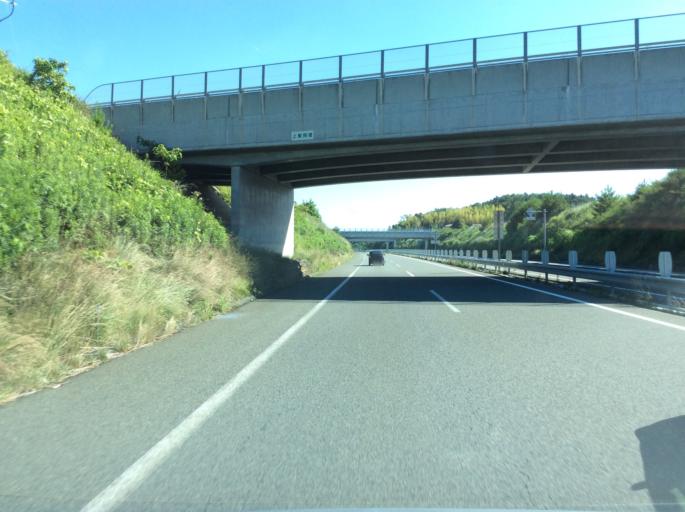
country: JP
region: Fukushima
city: Namie
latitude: 37.3032
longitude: 140.9898
